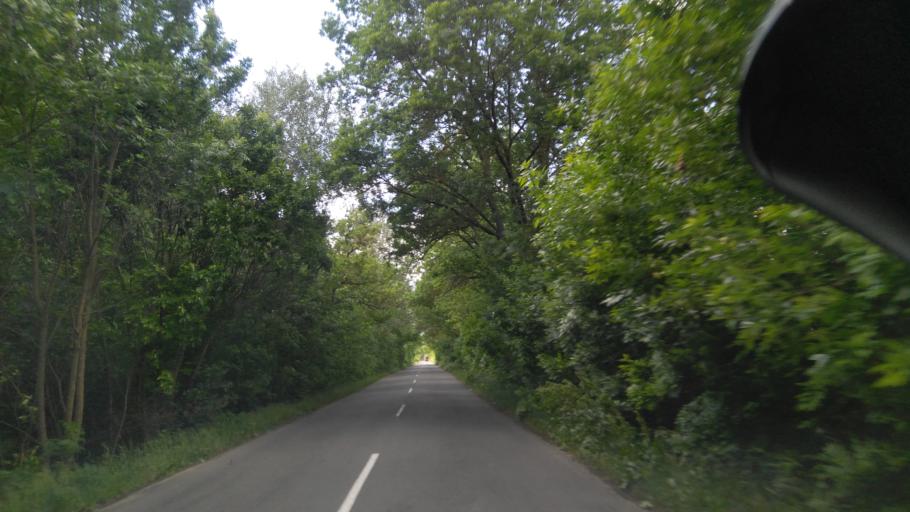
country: HU
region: Bekes
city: Bucsa
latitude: 47.1820
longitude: 21.0465
